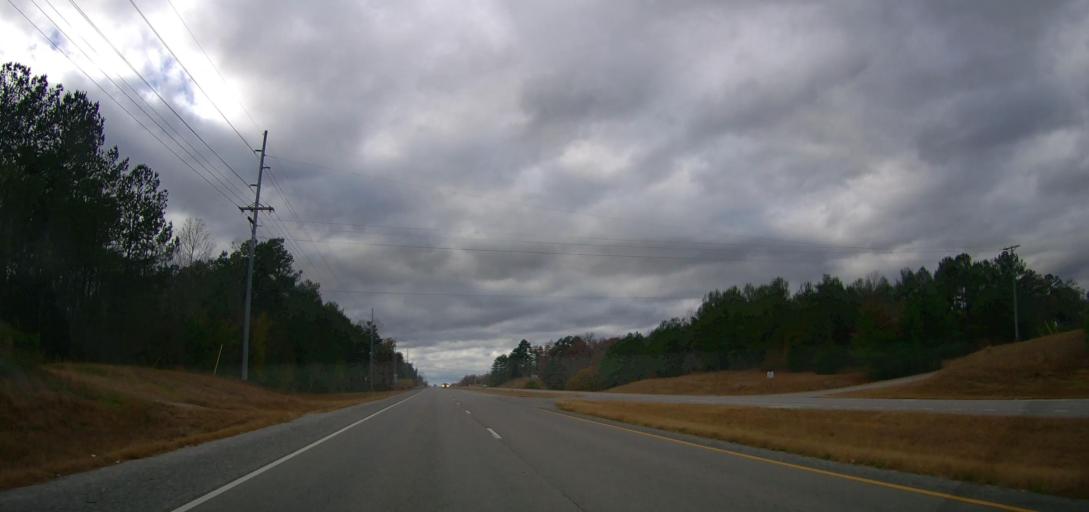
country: US
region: Alabama
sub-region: Lawrence County
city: Moulton
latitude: 34.5644
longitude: -87.3614
